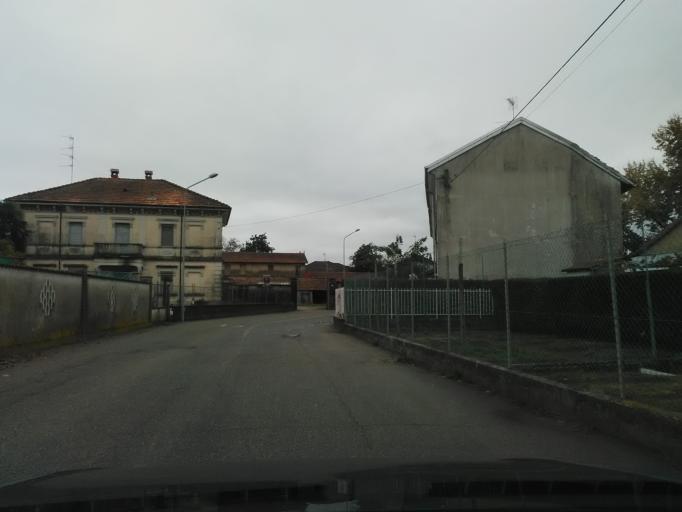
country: IT
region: Piedmont
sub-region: Provincia di Vercelli
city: Olcenengo
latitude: 45.3606
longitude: 8.3095
